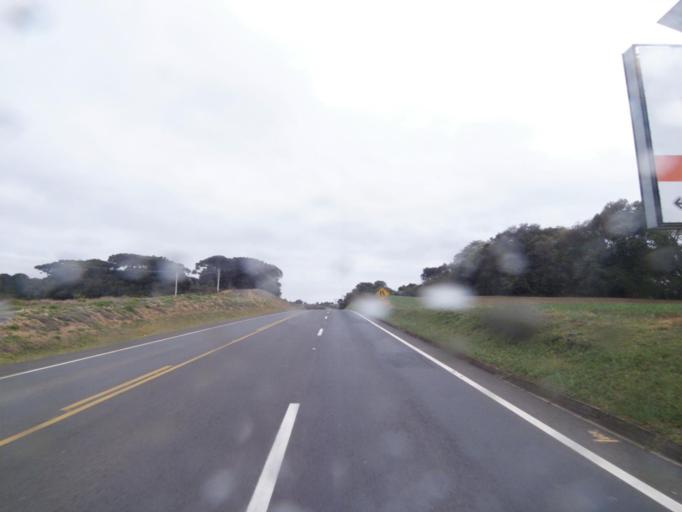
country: BR
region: Parana
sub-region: Palmeira
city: Palmeira
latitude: -25.4276
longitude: -50.1243
